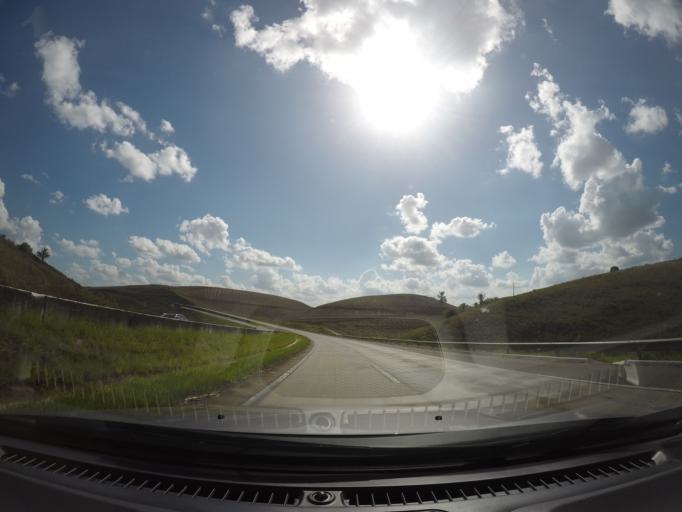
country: BR
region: Pernambuco
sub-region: Ribeirao
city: Ribeirao
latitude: -8.4984
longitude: -35.3869
